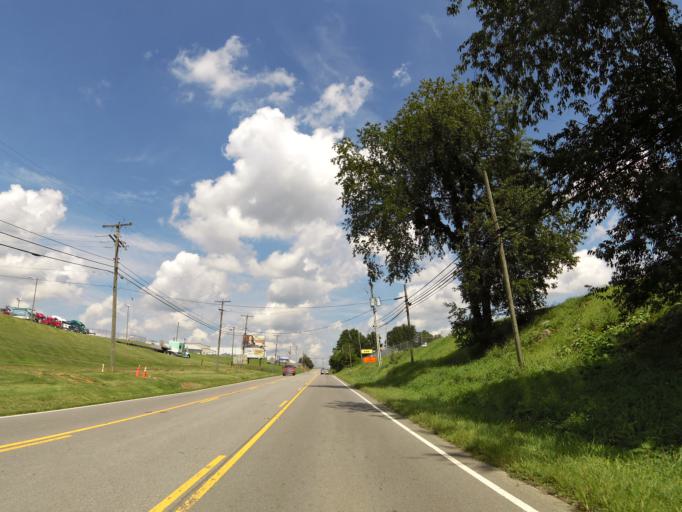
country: US
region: Virginia
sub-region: Washington County
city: Abingdon
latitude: 36.6795
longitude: -82.0403
